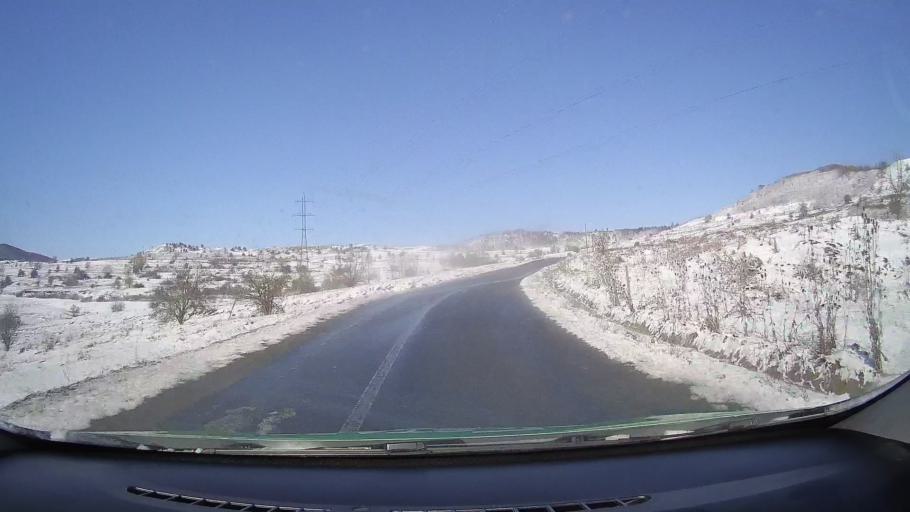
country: RO
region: Sibiu
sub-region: Comuna Avrig
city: Avrig
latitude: 45.7698
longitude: 24.3850
